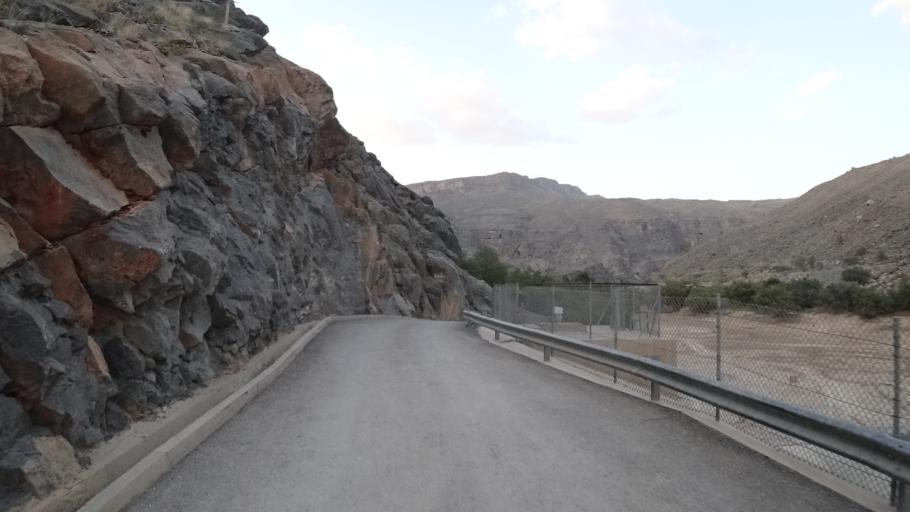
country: OM
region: Muhafazat ad Dakhiliyah
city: Nizwa
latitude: 23.0584
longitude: 57.4684
